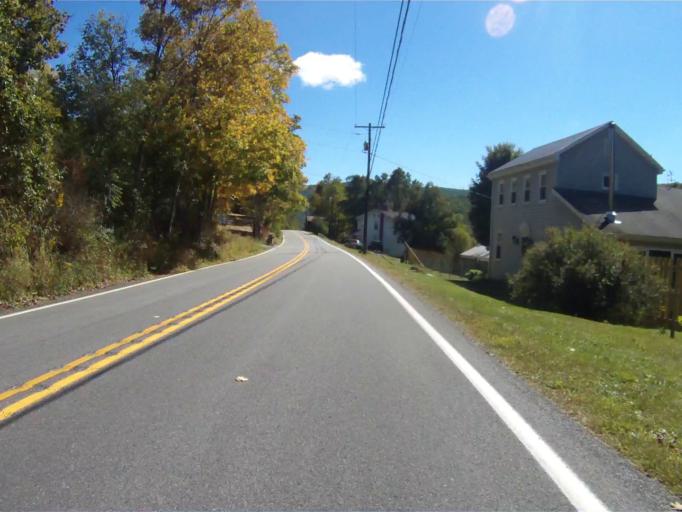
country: US
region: Pennsylvania
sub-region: Centre County
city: Milesburg
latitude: 40.9143
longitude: -77.8888
